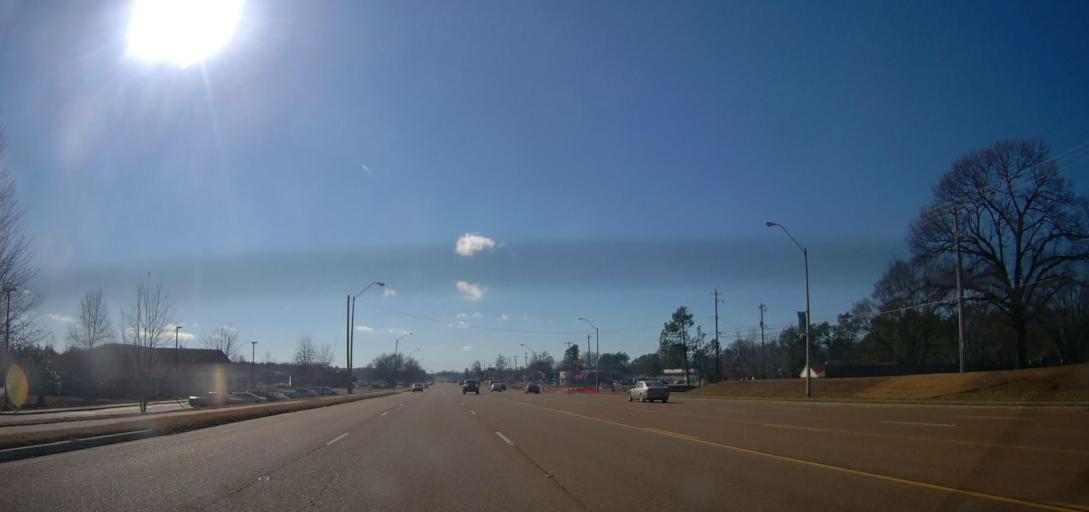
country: US
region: Tennessee
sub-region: Shelby County
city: Bartlett
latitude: 35.2243
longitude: -89.9059
